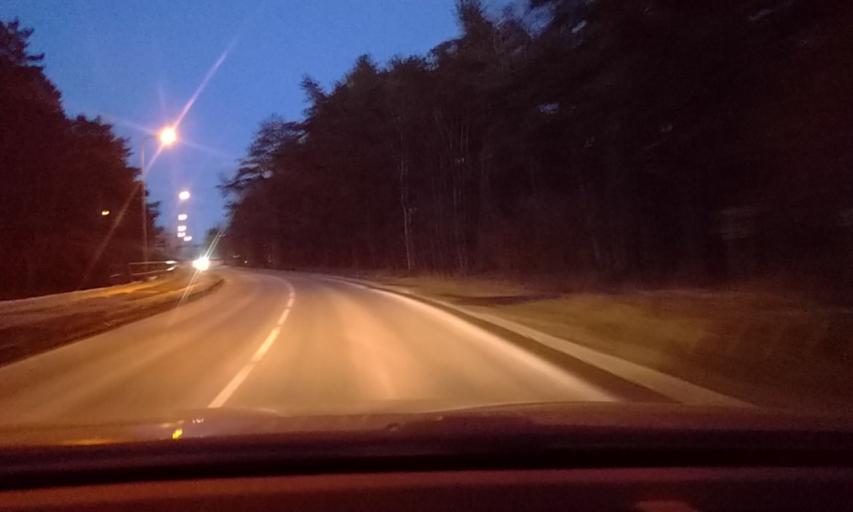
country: EE
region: Harju
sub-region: Viimsi vald
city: Viimsi
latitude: 59.4850
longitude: 24.8624
